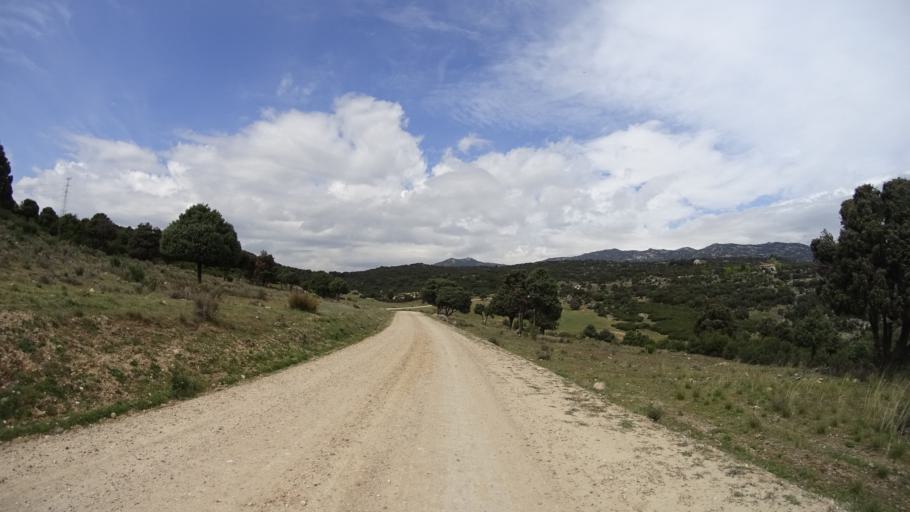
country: ES
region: Madrid
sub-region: Provincia de Madrid
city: Hoyo de Manzanares
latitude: 40.6180
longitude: -3.8782
